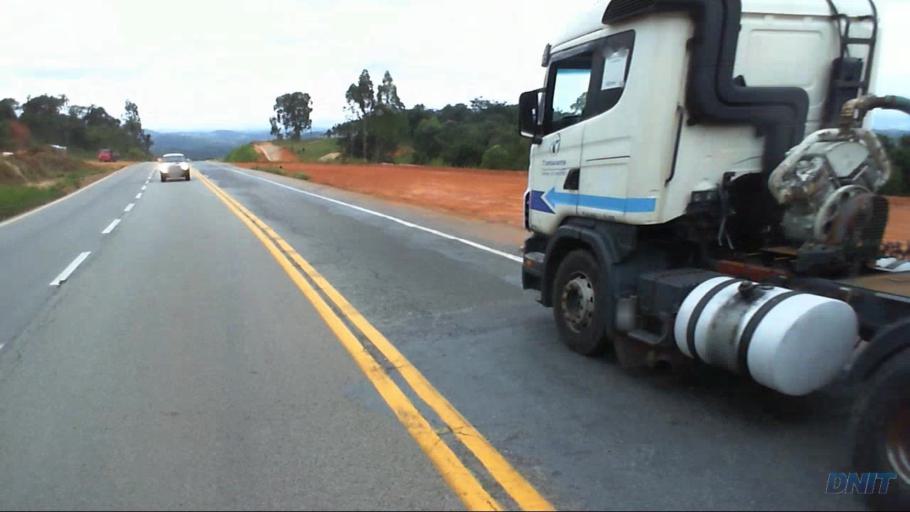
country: BR
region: Minas Gerais
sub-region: Caete
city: Caete
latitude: -19.7503
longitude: -43.5237
